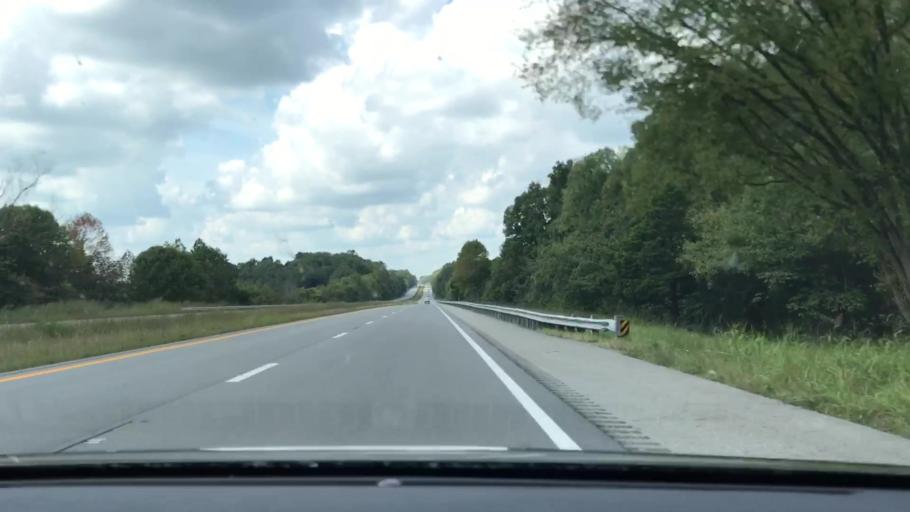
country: US
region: Kentucky
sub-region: Adair County
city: Columbia
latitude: 37.0782
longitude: -85.2373
